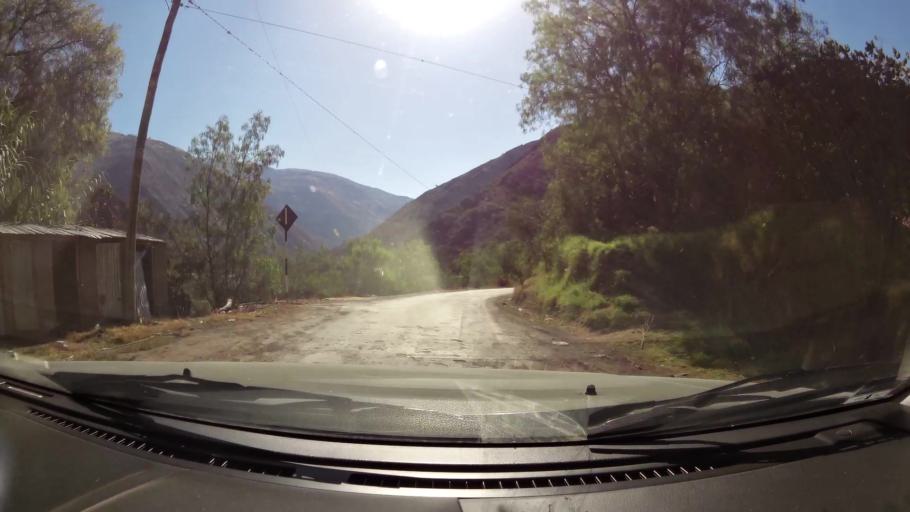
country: PE
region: Huancavelica
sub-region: Provincia de Acobamba
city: Pomacocha
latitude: -12.7673
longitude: -74.5066
